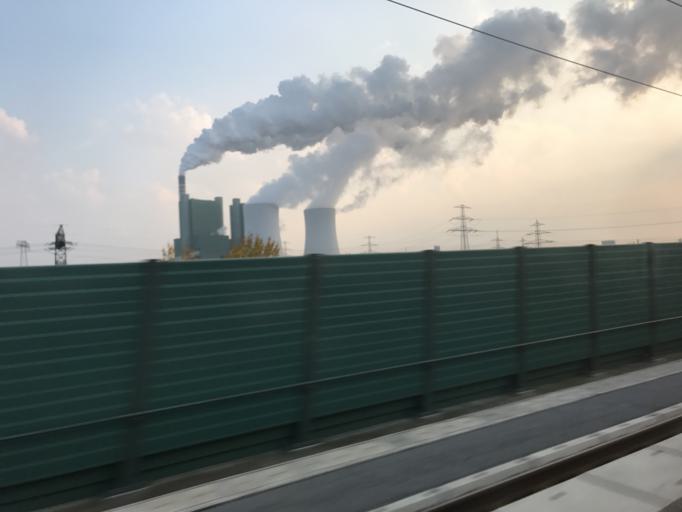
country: DE
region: Saxony-Anhalt
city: Schkopau
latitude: 51.4082
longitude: 11.9519
